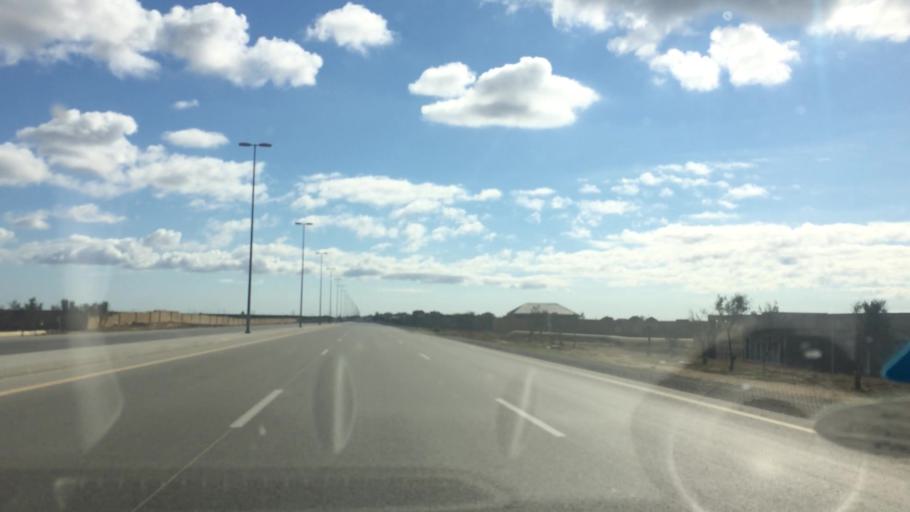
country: AZ
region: Baki
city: Qala
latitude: 40.4554
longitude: 50.1453
